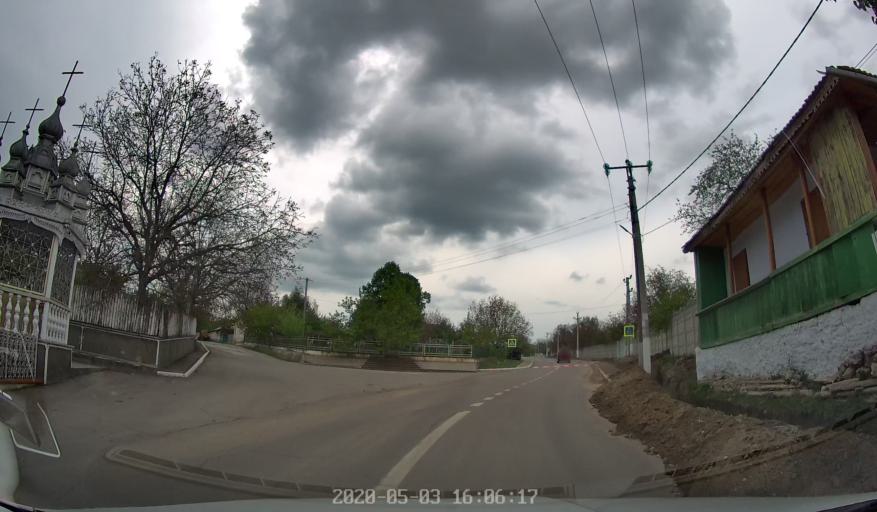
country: MD
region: Calarasi
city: Calarasi
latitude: 47.1927
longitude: 28.3521
